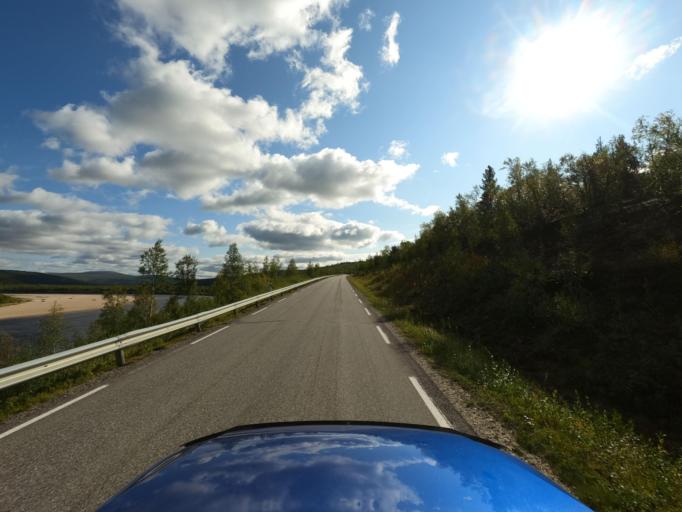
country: NO
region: Finnmark Fylke
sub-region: Karasjok
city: Karasjohka
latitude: 69.4428
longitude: 25.6355
